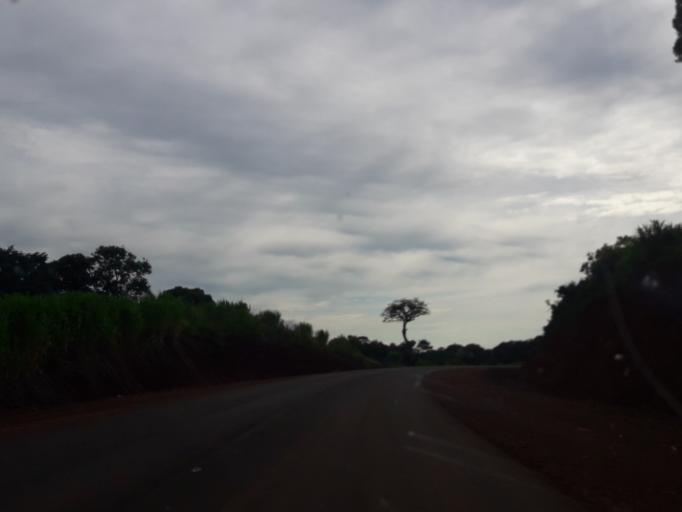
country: AR
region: Misiones
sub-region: Departamento de San Pedro
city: San Pedro
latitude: -26.5089
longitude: -53.9216
